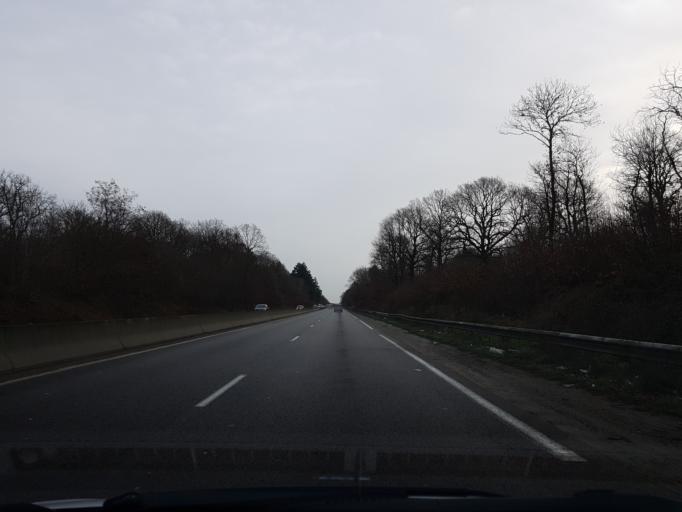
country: FR
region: Ile-de-France
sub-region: Departement de l'Essonne
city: Montgeron
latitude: 48.6903
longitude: 2.4587
